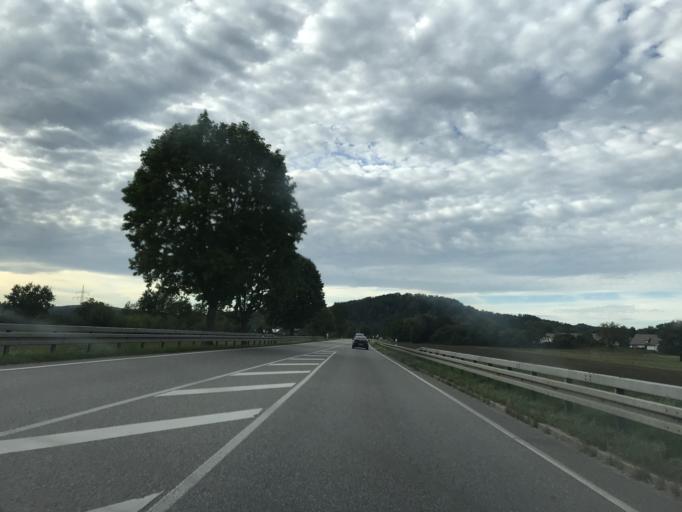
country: CH
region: Aargau
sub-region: Bezirk Rheinfelden
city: Mumpf
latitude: 47.5757
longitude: 7.9141
